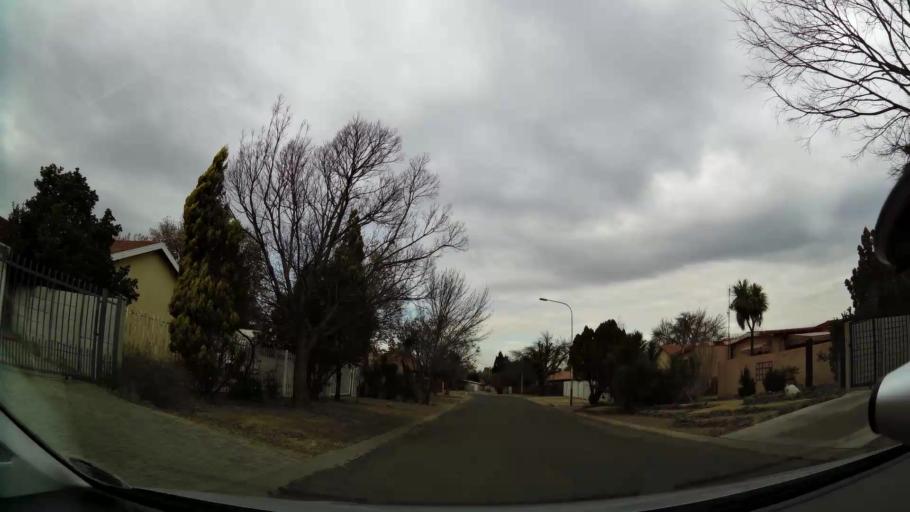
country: ZA
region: Orange Free State
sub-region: Fezile Dabi District Municipality
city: Kroonstad
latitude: -27.6512
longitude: 27.2459
